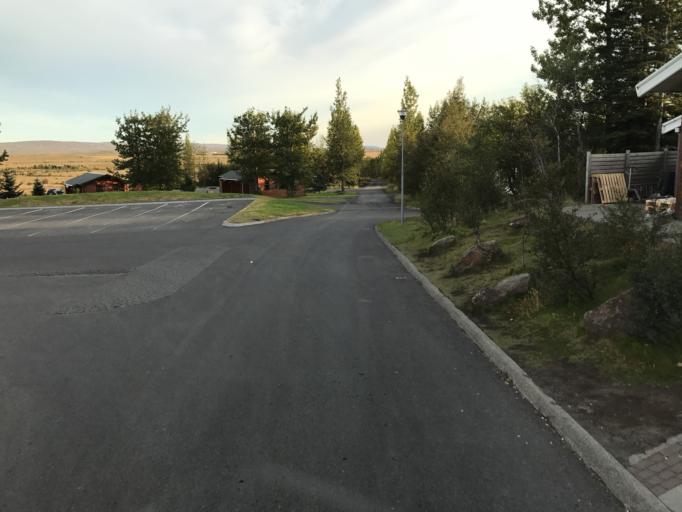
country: IS
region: South
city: Selfoss
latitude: 64.3095
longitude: -20.3011
